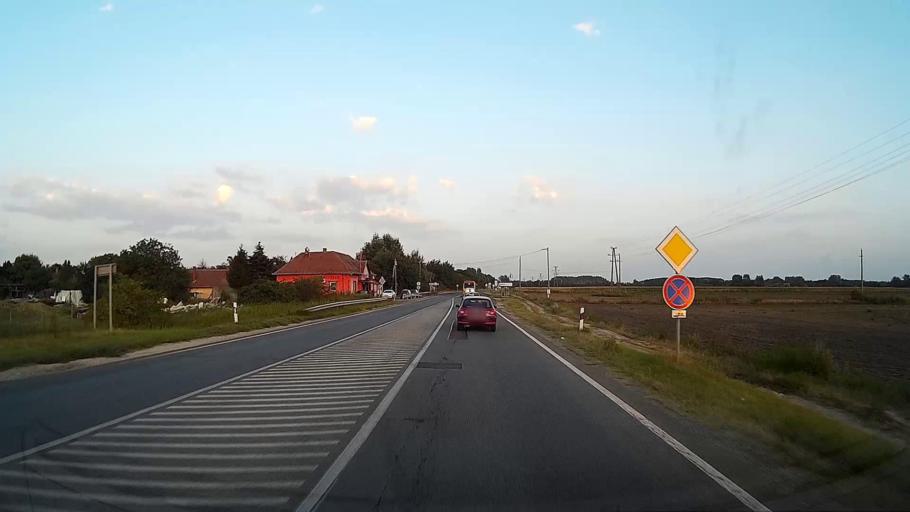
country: HU
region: Pest
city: Ullo
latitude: 47.3643
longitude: 19.3839
